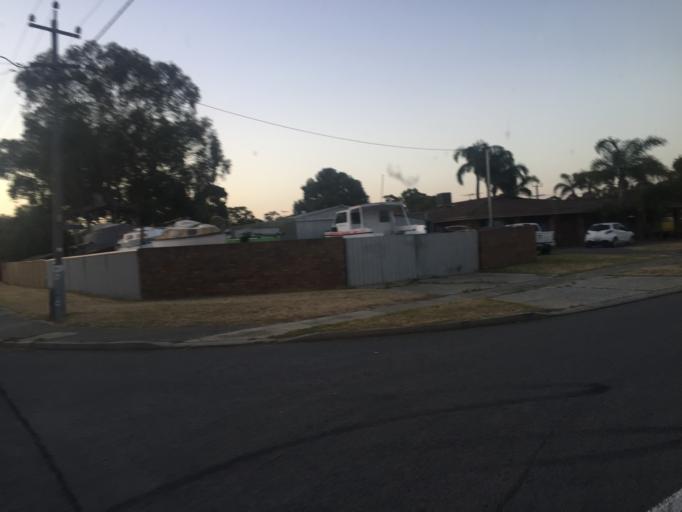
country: AU
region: Western Australia
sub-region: Gosnells
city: Maddington
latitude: -32.0322
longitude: 115.9937
